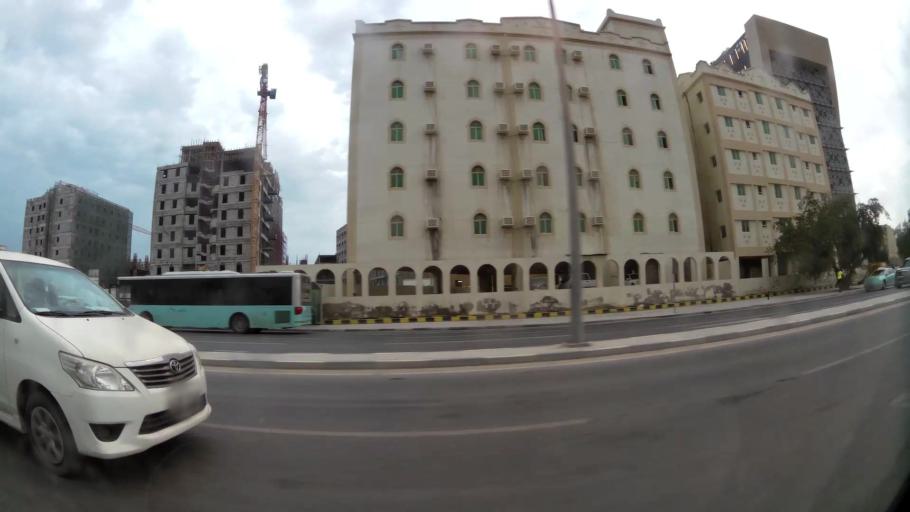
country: QA
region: Baladiyat ad Dawhah
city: Doha
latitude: 25.2673
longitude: 51.5259
